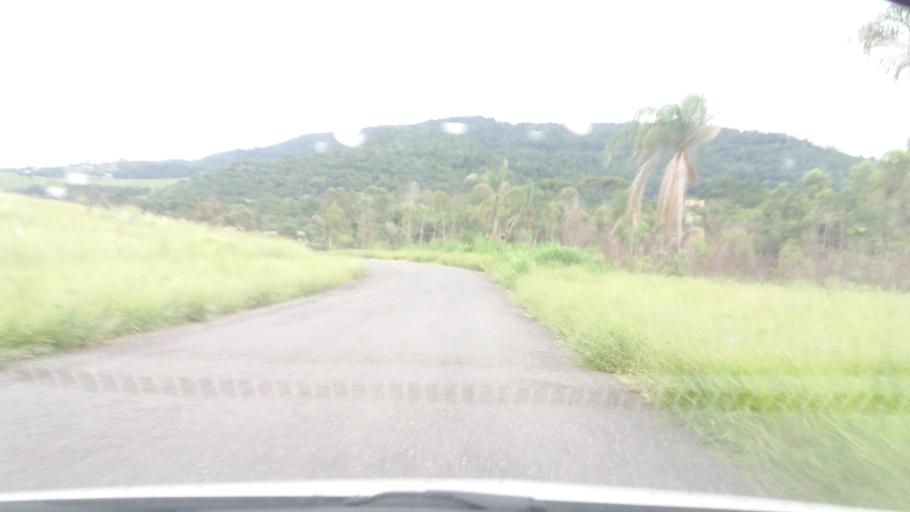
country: BR
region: Sao Paulo
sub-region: Bom Jesus Dos Perdoes
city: Bom Jesus dos Perdoes
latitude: -23.1732
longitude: -46.4386
